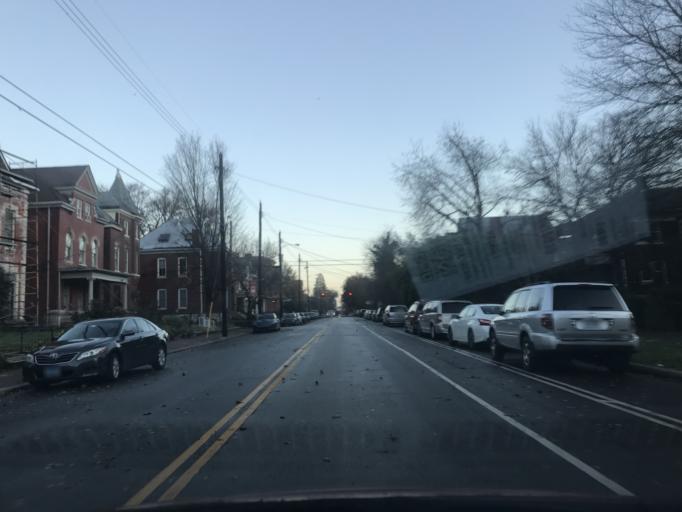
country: US
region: Kentucky
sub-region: Jefferson County
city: Louisville
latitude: 38.2304
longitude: -85.7544
